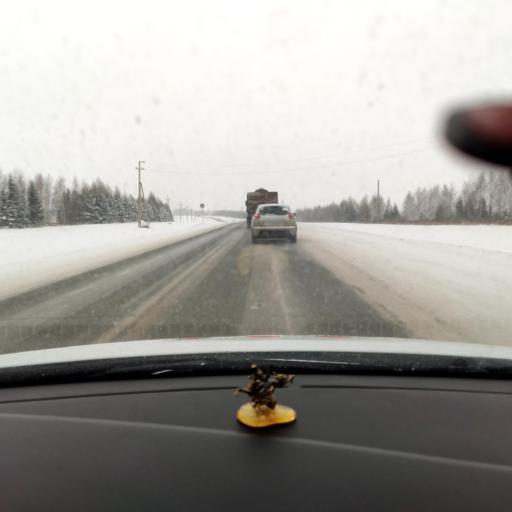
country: RU
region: Tatarstan
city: Vysokaya Gora
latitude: 56.0247
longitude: 49.2560
